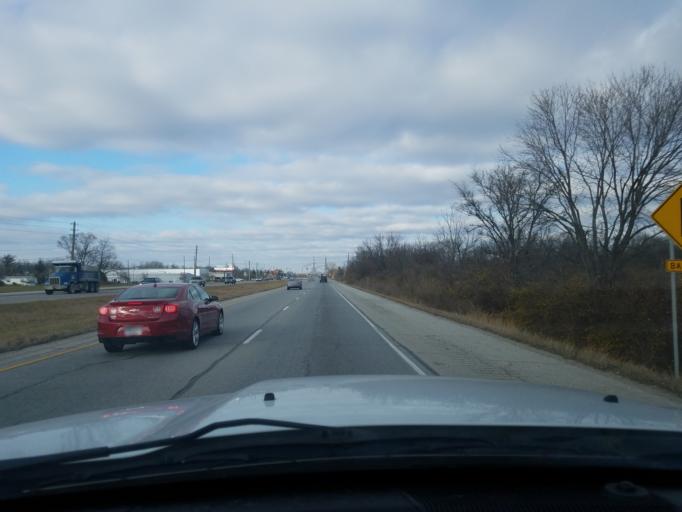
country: US
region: Indiana
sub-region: Marion County
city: Southport
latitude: 39.6684
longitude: -86.1959
